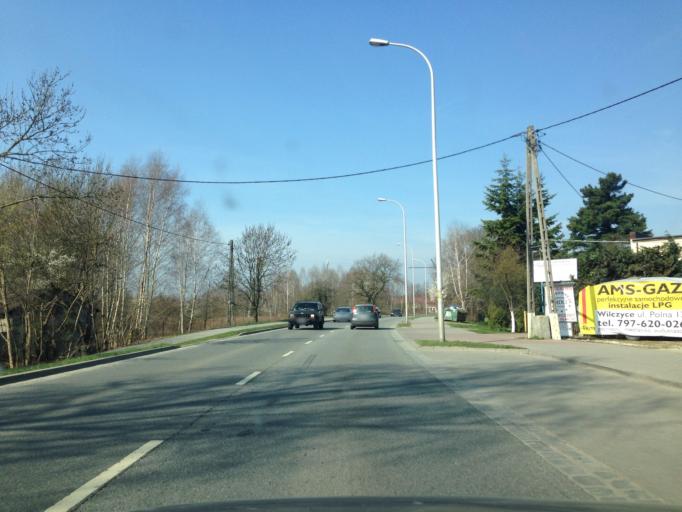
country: PL
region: Lower Silesian Voivodeship
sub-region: Powiat wroclawski
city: Wilczyce
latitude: 51.1040
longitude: 17.1510
